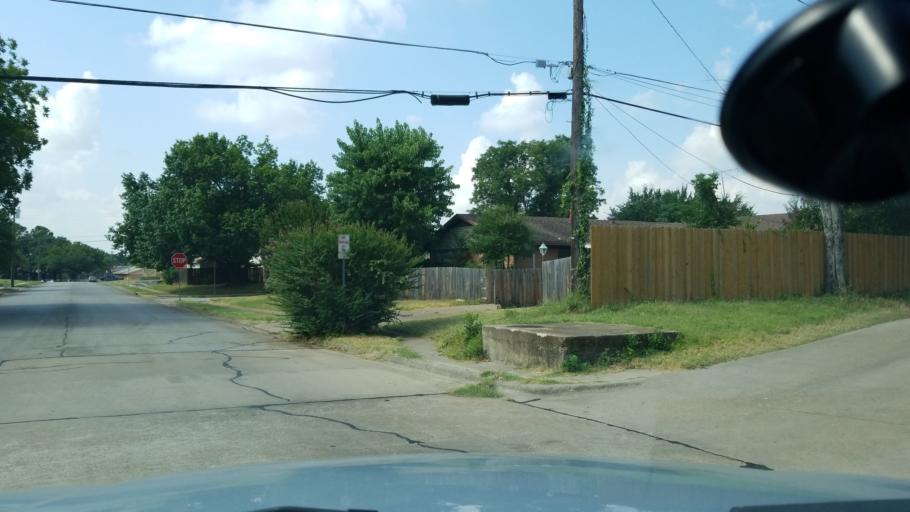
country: US
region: Texas
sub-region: Dallas County
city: Irving
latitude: 32.8333
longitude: -96.9276
